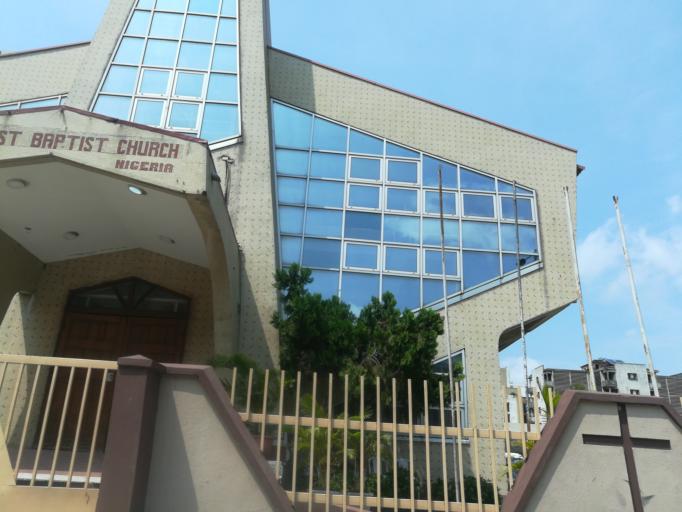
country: NG
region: Lagos
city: Lagos
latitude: 6.4493
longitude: 3.3947
